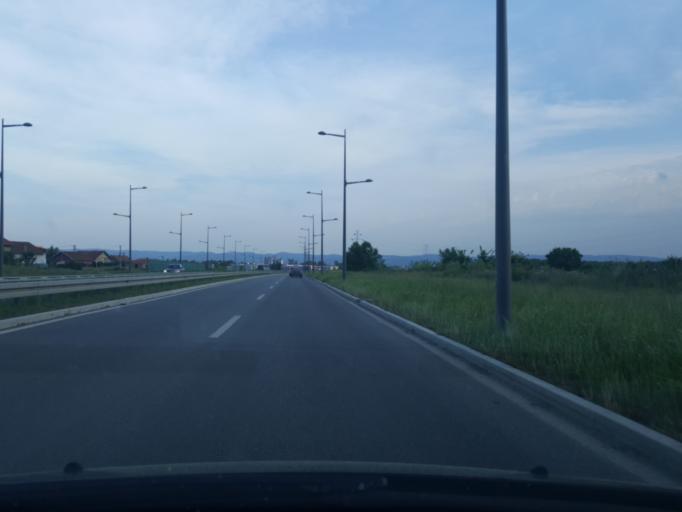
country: RS
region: Autonomna Pokrajina Vojvodina
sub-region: Juznobacki Okrug
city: Novi Sad
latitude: 45.2968
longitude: 19.8077
